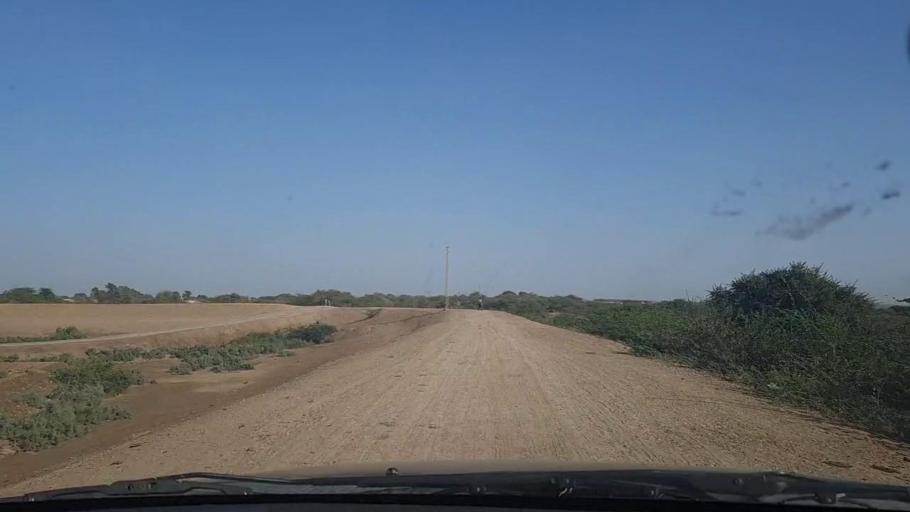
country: PK
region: Sindh
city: Chuhar Jamali
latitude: 24.3669
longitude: 67.7775
